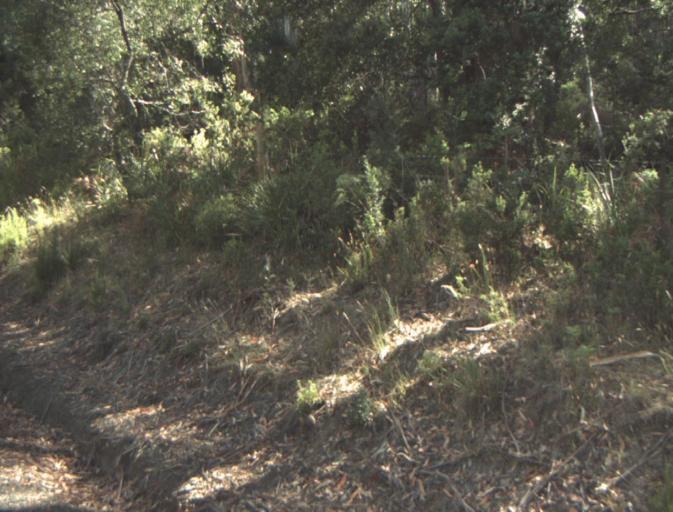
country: AU
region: Tasmania
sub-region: Launceston
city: Newstead
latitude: -41.3266
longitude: 147.3419
